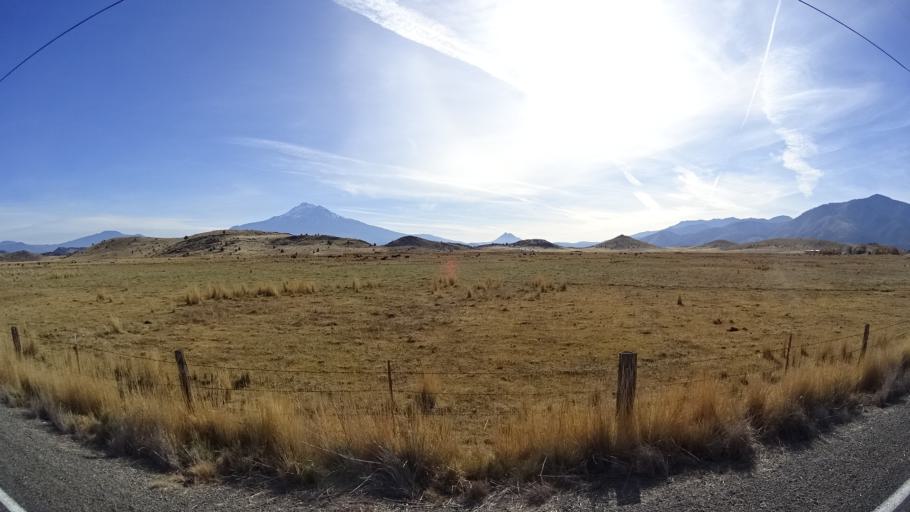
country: US
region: California
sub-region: Siskiyou County
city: Weed
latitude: 41.5350
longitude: -122.5096
